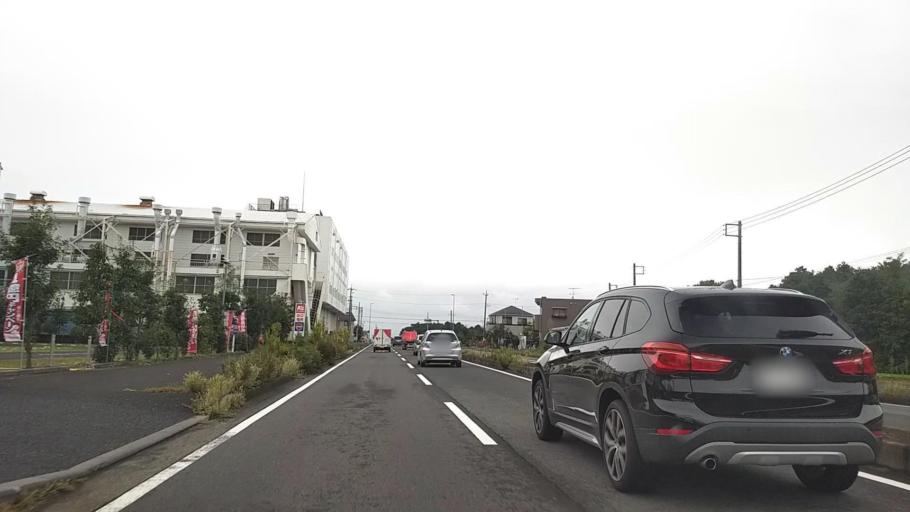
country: JP
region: Kanagawa
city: Atsugi
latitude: 35.4041
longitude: 139.4241
